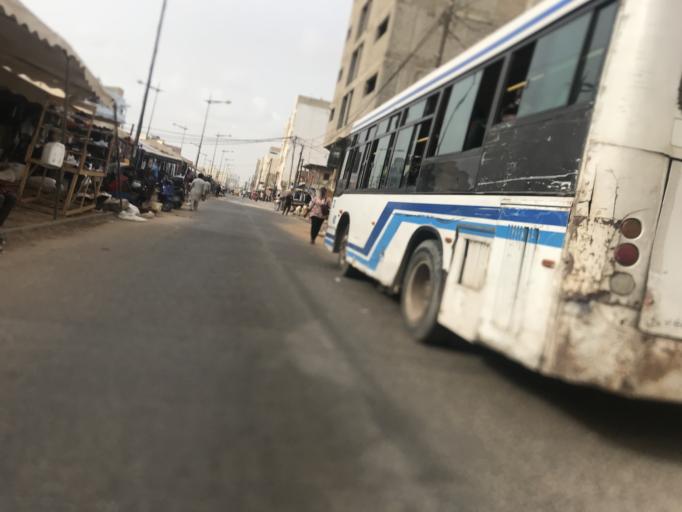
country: SN
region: Dakar
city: Dakar
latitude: 14.6814
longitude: -17.4549
